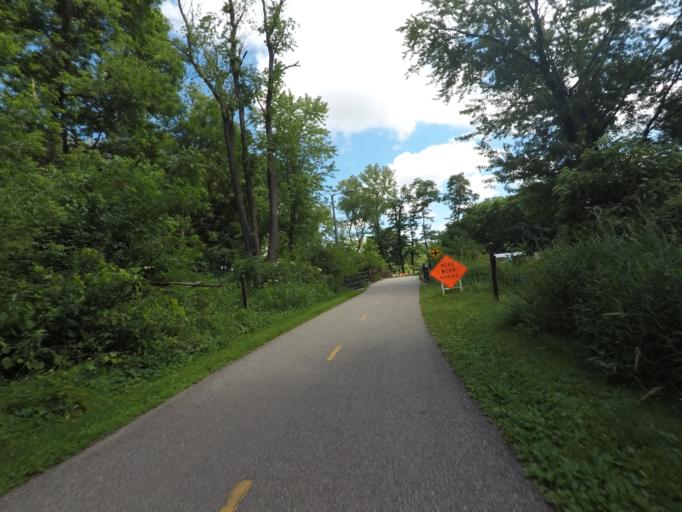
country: US
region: Wisconsin
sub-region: Dane County
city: Verona
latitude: 43.0234
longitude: -89.5255
